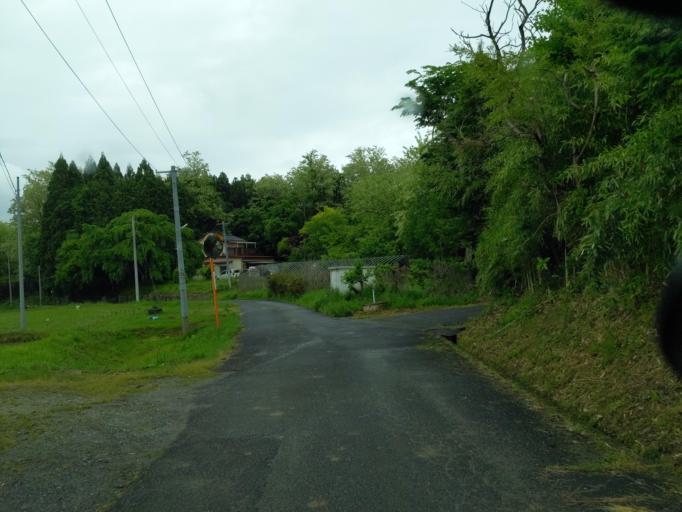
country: JP
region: Fukushima
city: Koriyama
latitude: 37.3424
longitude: 140.3920
